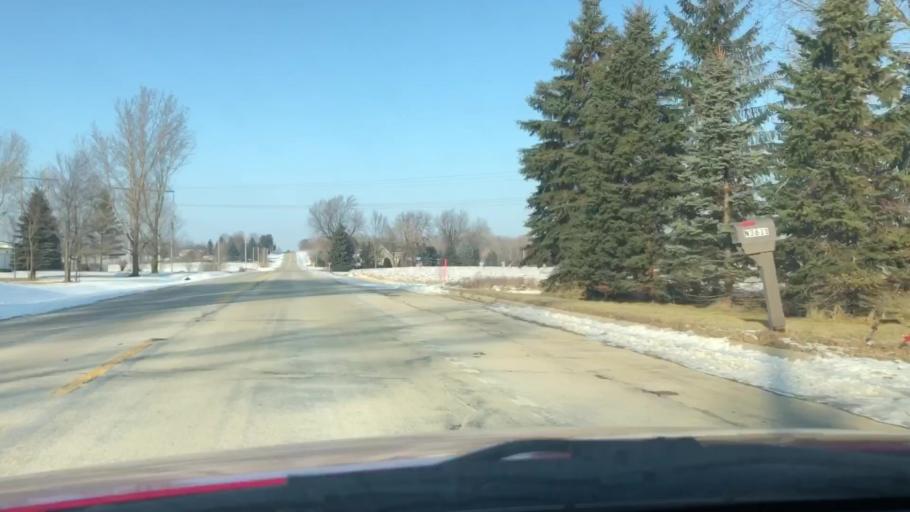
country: US
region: Wisconsin
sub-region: Outagamie County
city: Kimberly
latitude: 44.3693
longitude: -88.3749
